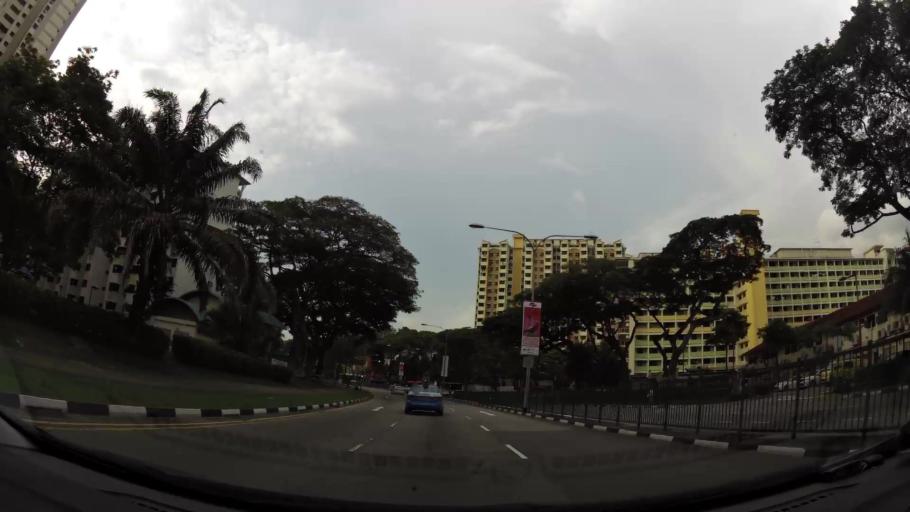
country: SG
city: Singapore
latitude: 1.3349
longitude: 103.8561
